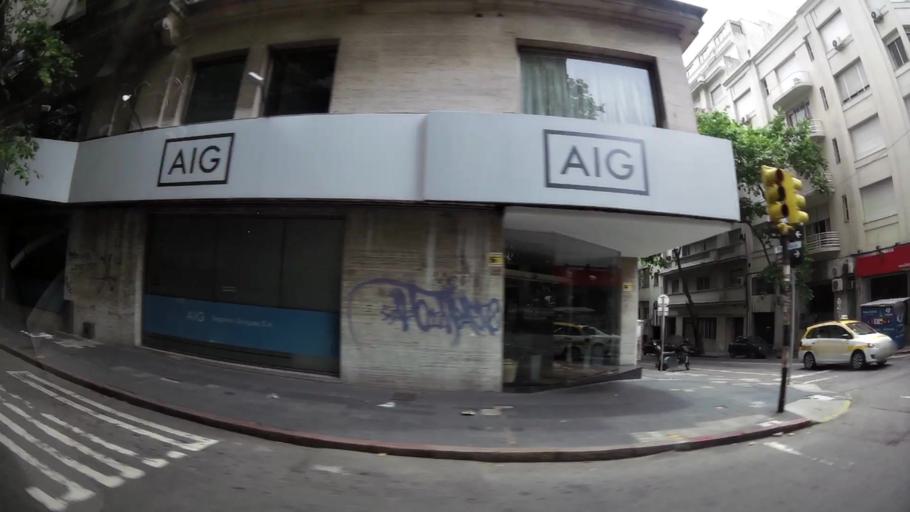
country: UY
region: Montevideo
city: Montevideo
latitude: -34.9052
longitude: -56.1948
